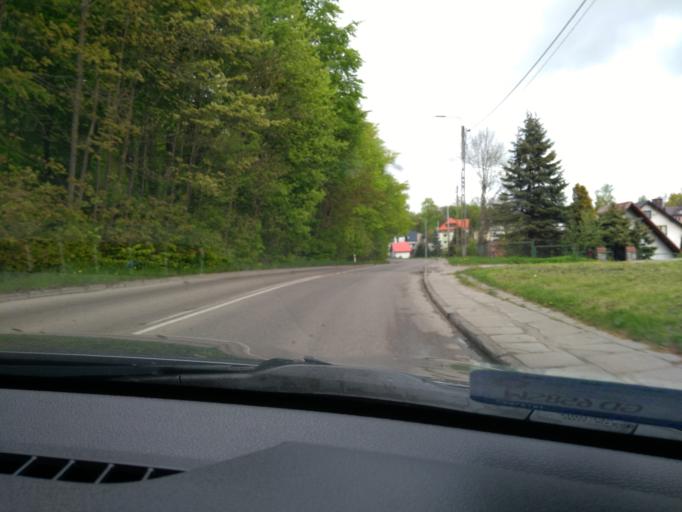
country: PL
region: Pomeranian Voivodeship
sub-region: Powiat kartuski
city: Kartuzy
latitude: 54.3394
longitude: 18.1822
